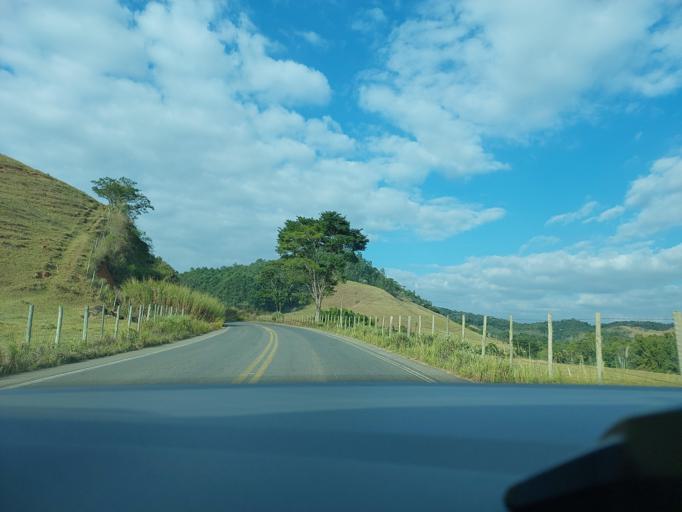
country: BR
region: Minas Gerais
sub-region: Vicosa
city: Vicosa
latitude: -20.8316
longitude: -42.7576
